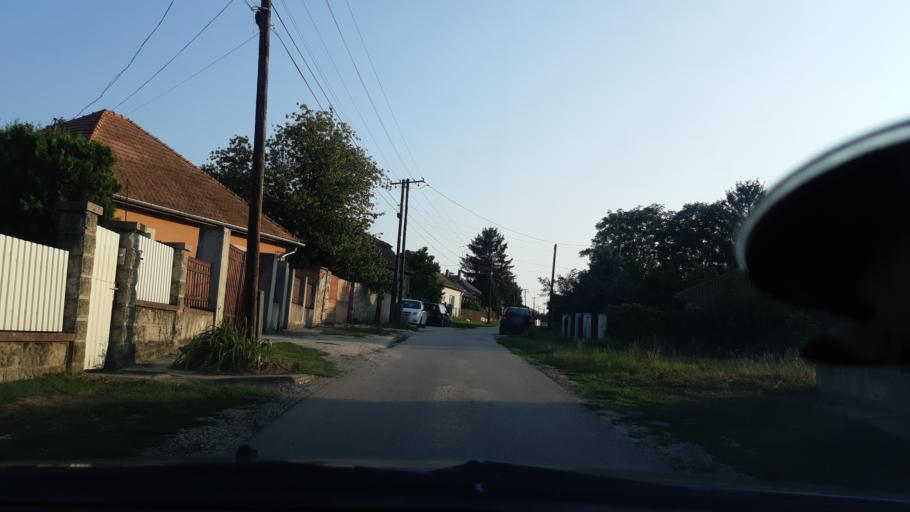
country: HU
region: Fejer
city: Bicske
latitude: 47.4888
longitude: 18.6452
